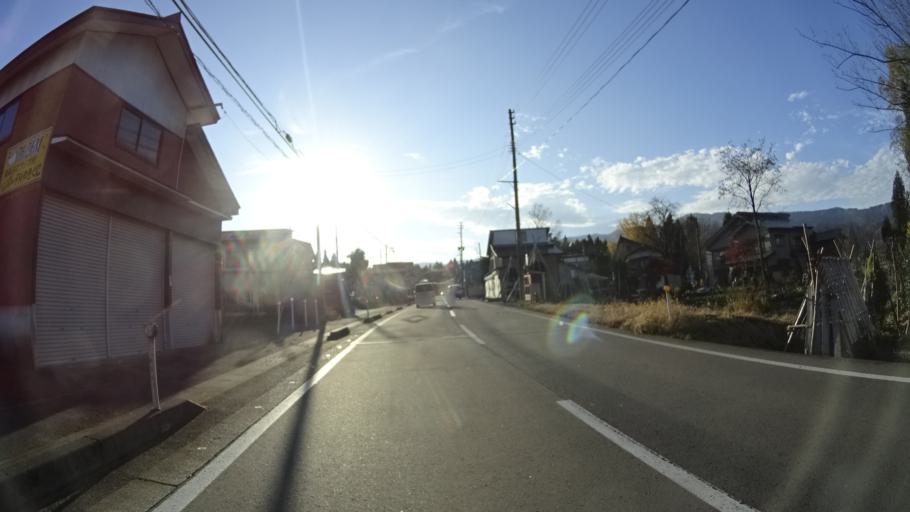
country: JP
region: Niigata
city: Shiozawa
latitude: 37.0024
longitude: 138.8331
